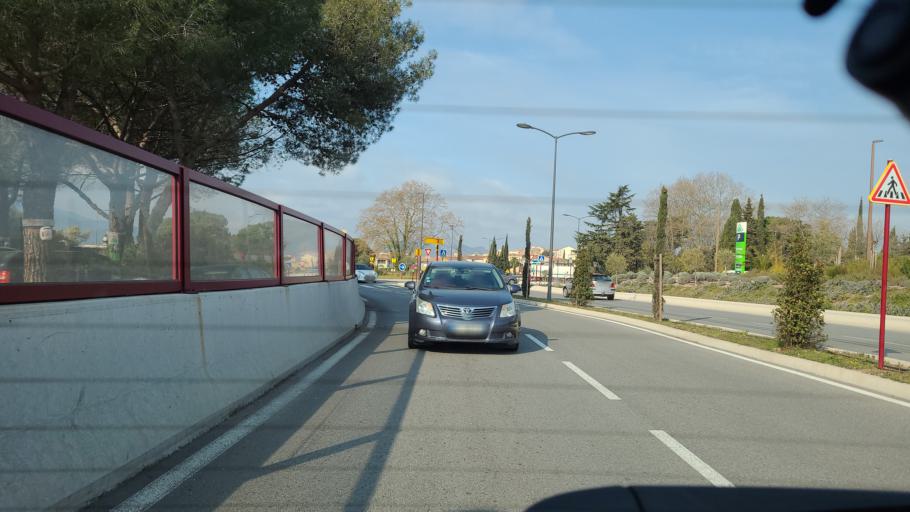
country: FR
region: Provence-Alpes-Cote d'Azur
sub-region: Departement du Var
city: Puget-sur-Argens
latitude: 43.4556
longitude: 6.6925
